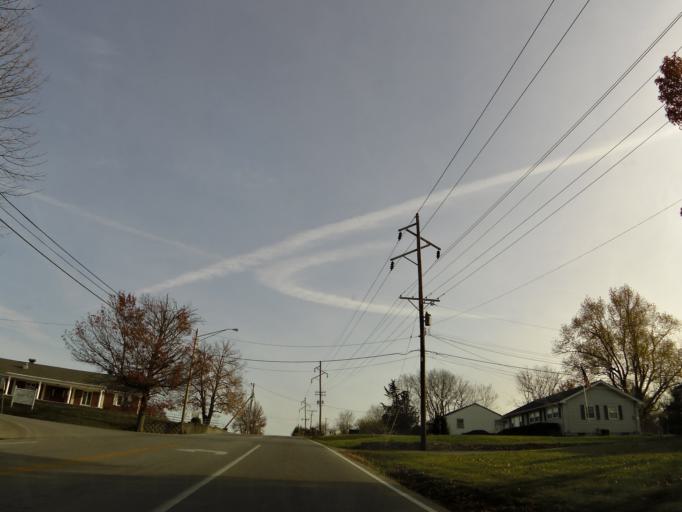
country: US
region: Kentucky
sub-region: Harrison County
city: Cynthiana
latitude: 38.3812
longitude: -84.2954
